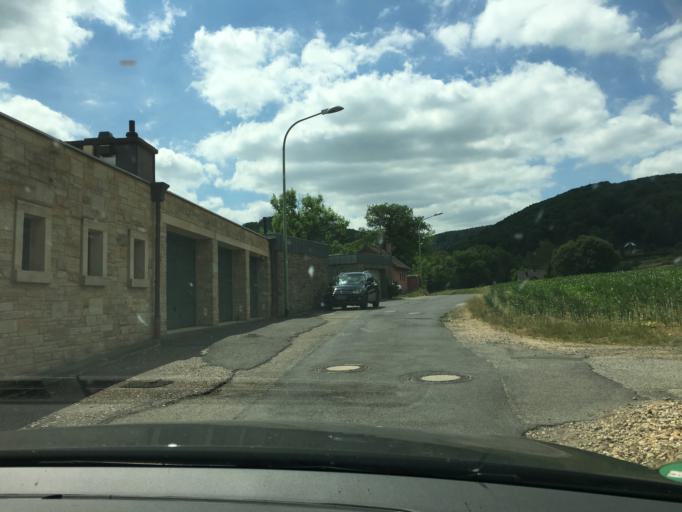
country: DE
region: North Rhine-Westphalia
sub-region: Regierungsbezirk Koln
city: Nideggen
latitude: 50.7138
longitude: 6.4401
